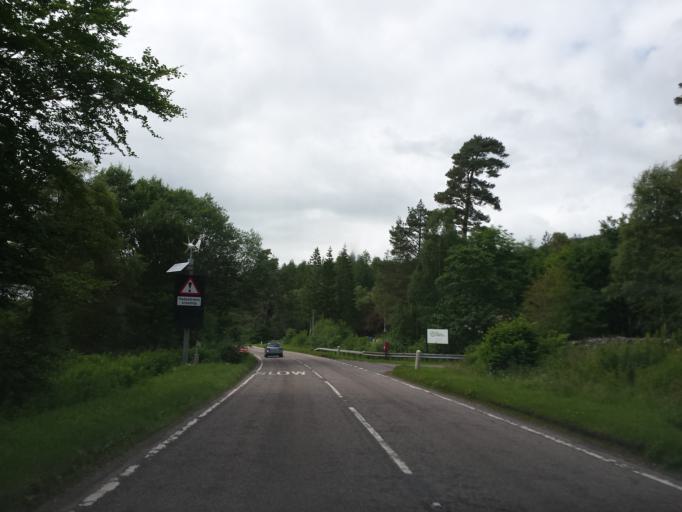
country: GB
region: Scotland
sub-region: Highland
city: Fort William
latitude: 56.8549
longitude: -5.1895
